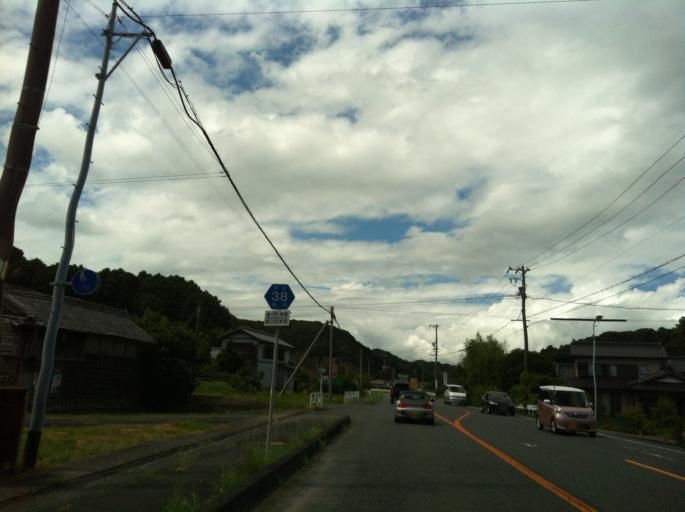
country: JP
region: Shizuoka
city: Kakegawa
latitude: 34.7244
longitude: 138.0479
